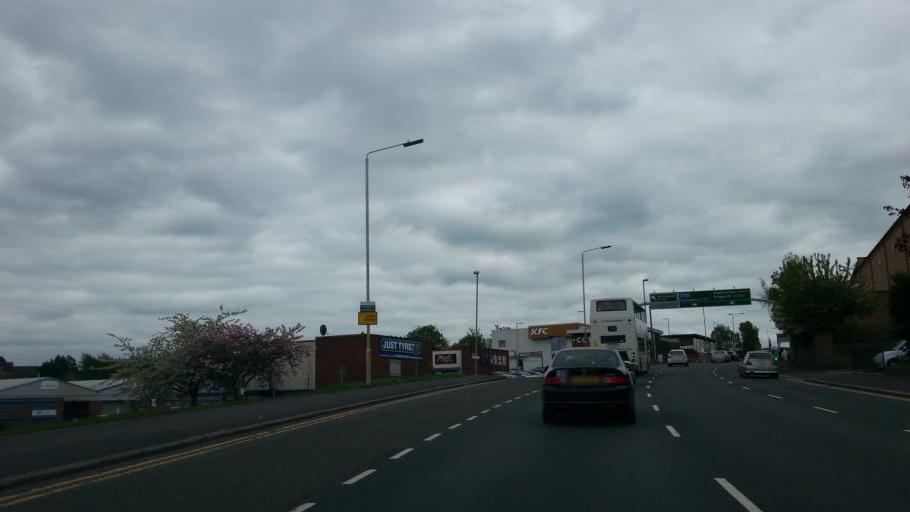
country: GB
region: England
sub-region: Dudley
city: Stourbridge
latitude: 52.4598
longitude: -2.1475
